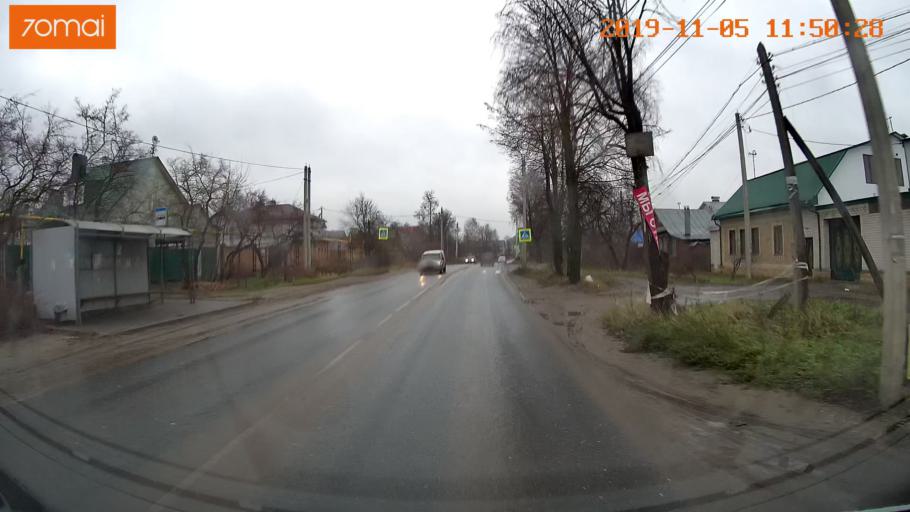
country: RU
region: Ivanovo
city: Bogorodskoye
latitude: 57.0070
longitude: 41.0170
